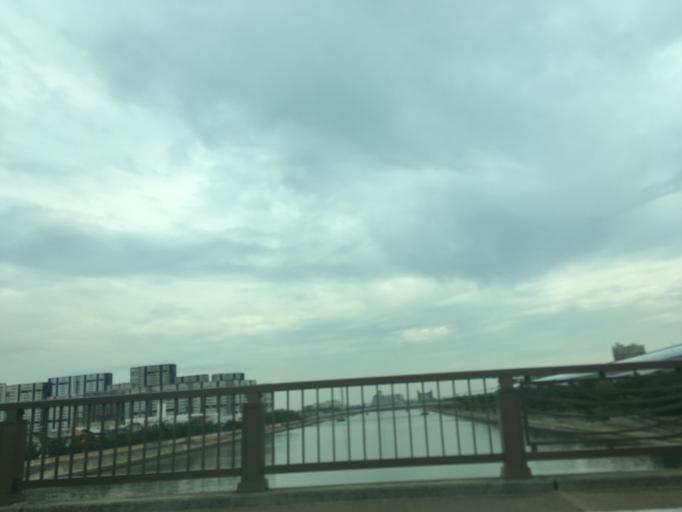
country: JP
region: Hyogo
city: Ashiya
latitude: 34.7144
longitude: 135.3090
